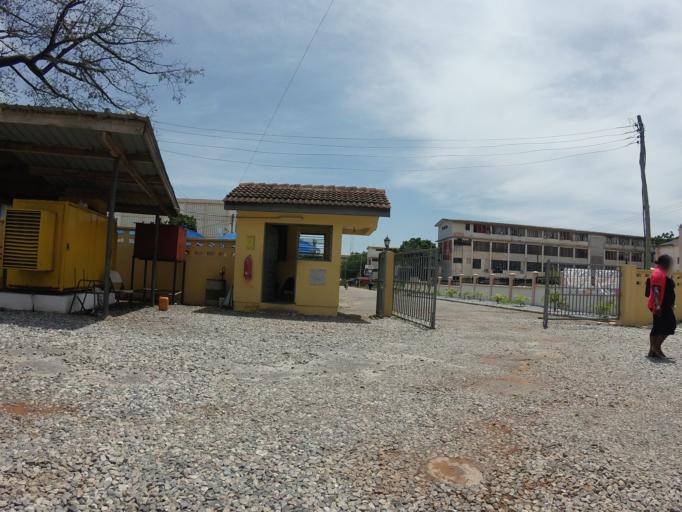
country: GH
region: Greater Accra
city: Accra
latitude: 5.5594
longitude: -0.2080
